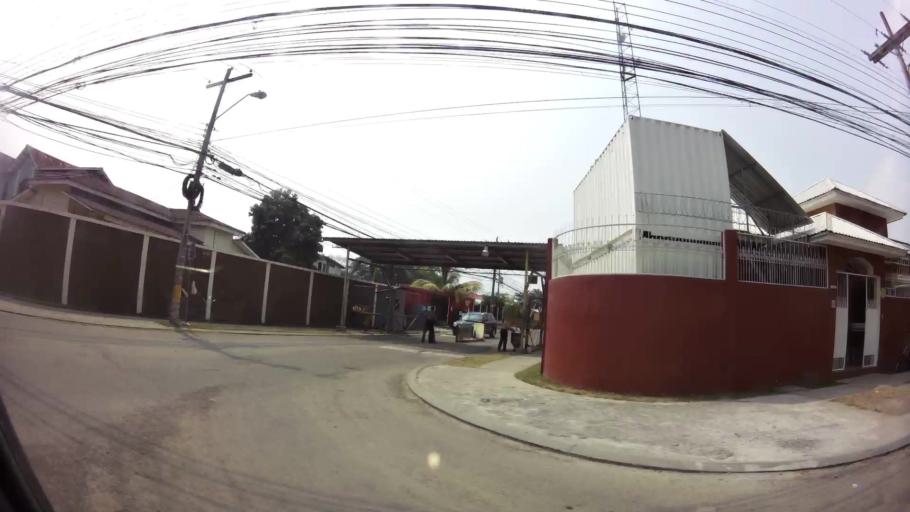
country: HN
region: Cortes
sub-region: San Pedro Sula
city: Pena Blanca
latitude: 15.5563
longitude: -88.0192
